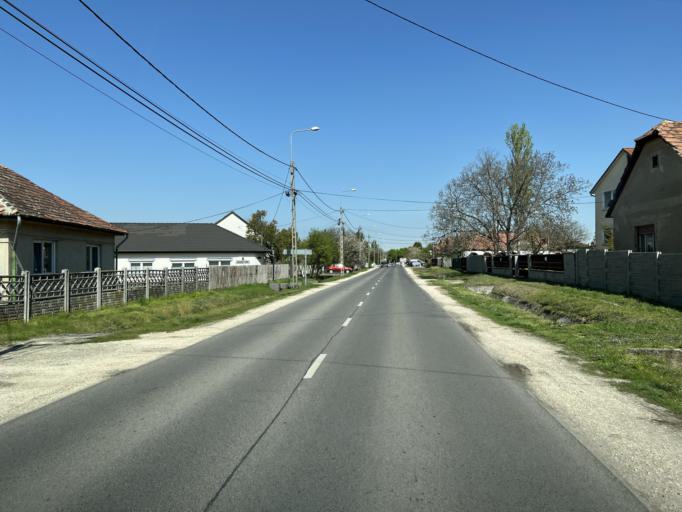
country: HU
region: Pest
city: Ocsa
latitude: 47.3007
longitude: 19.2203
